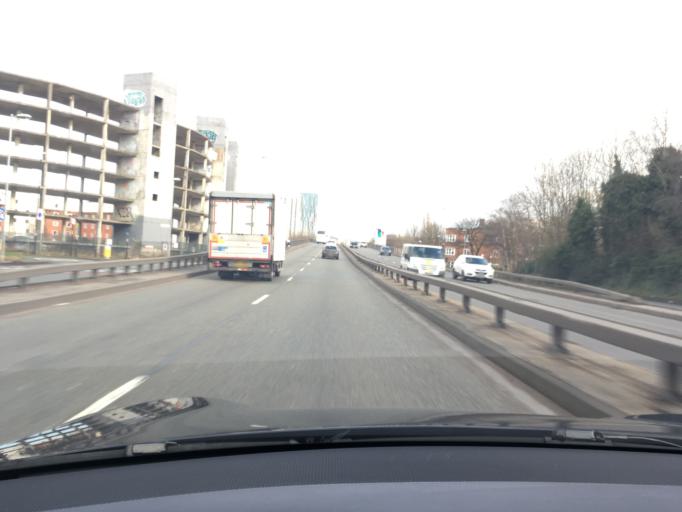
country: GB
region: England
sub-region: Manchester
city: Hulme
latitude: 53.4708
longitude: -2.2505
